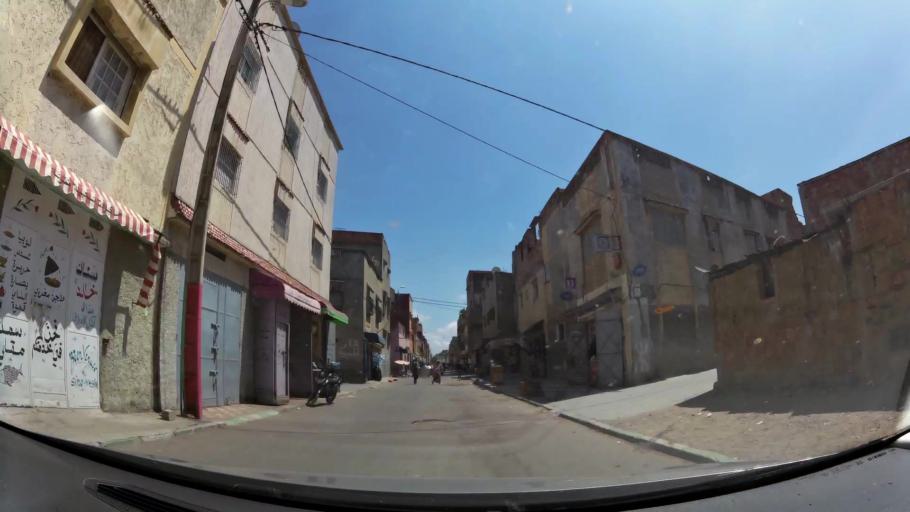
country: MA
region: Gharb-Chrarda-Beni Hssen
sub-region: Kenitra Province
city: Kenitra
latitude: 34.2522
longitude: -6.5550
